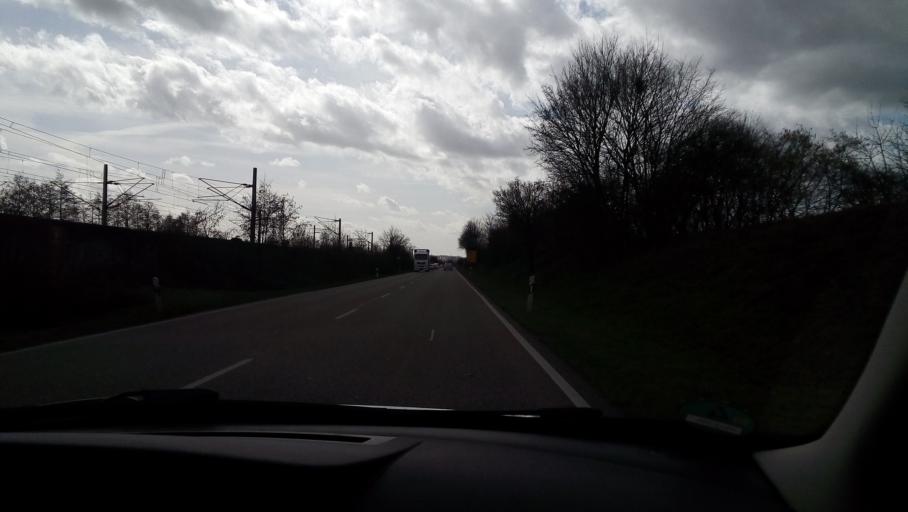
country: DE
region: Baden-Wuerttemberg
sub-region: Freiburg Region
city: Sasbach
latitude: 48.6527
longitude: 8.0861
